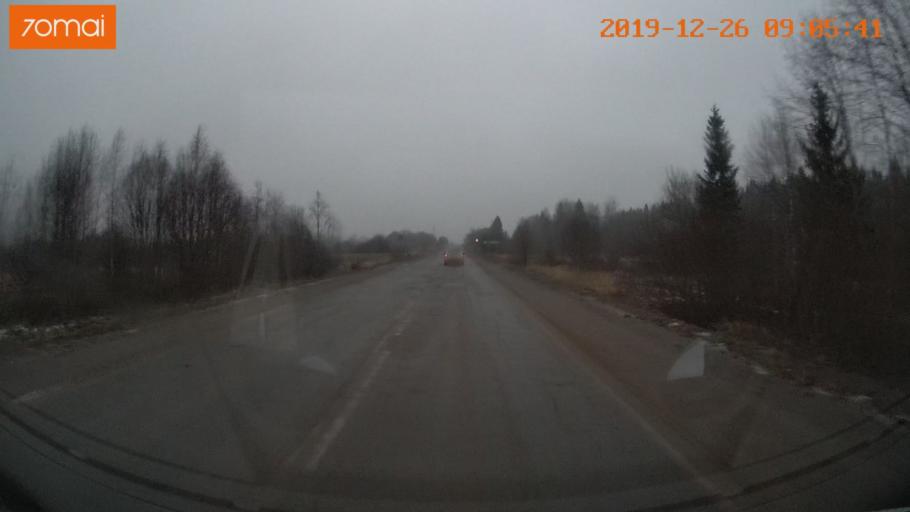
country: RU
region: Vologda
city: Gryazovets
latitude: 58.8281
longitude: 40.2569
